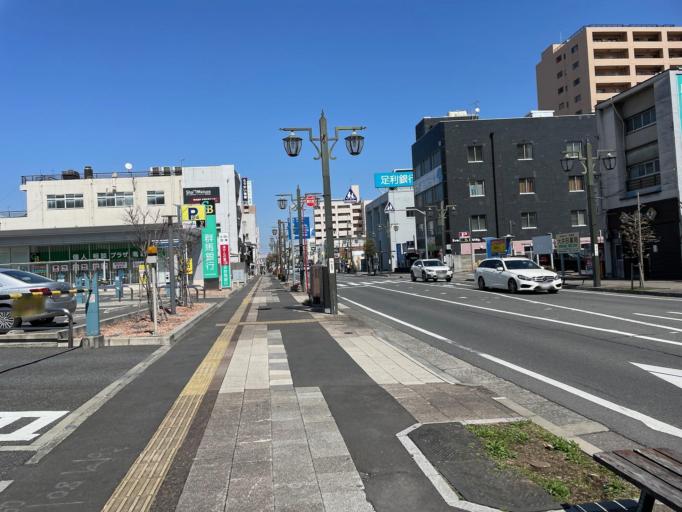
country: JP
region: Gunma
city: Takasaki
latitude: 36.3270
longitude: 139.0068
